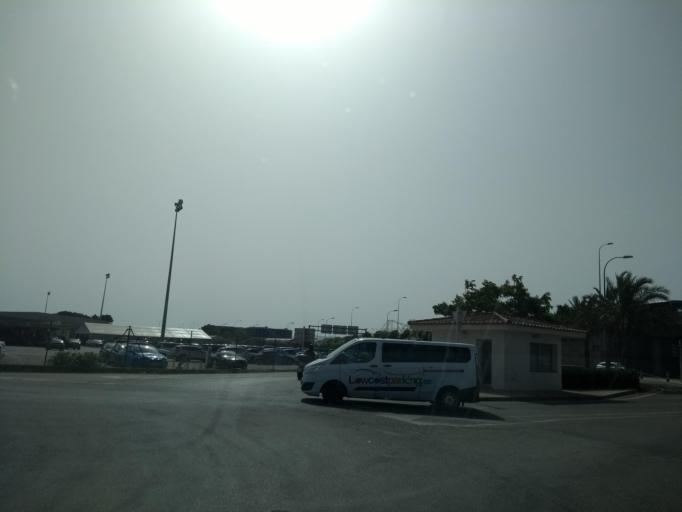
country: ES
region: Balearic Islands
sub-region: Illes Balears
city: s'Arenal
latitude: 39.5440
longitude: 2.7227
